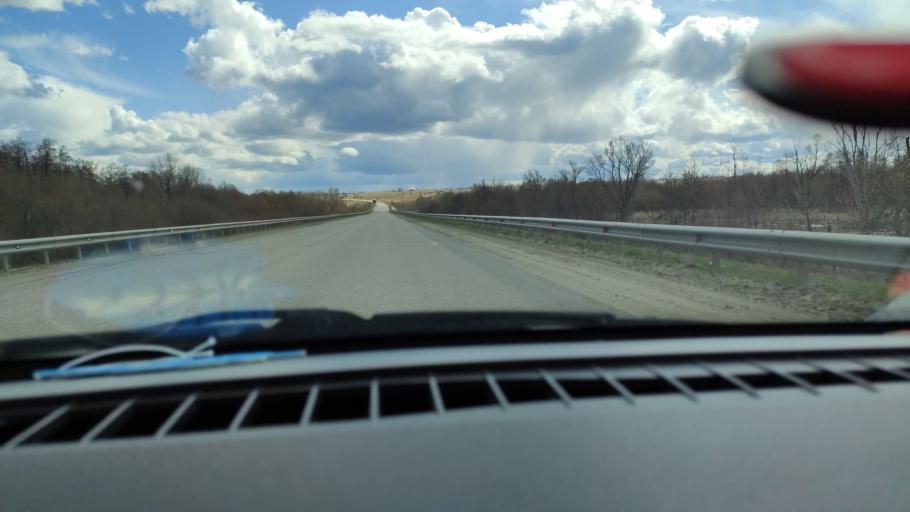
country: RU
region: Samara
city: Varlamovo
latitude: 53.1330
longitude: 48.2877
